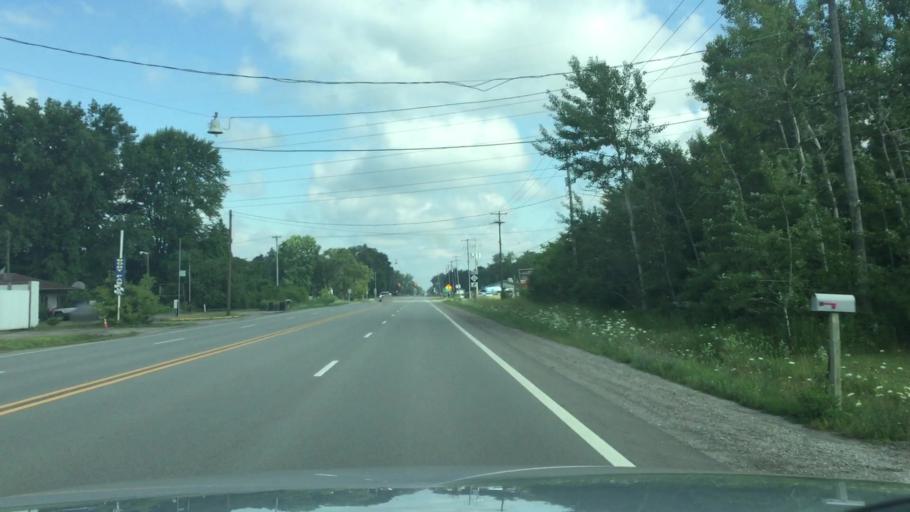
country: US
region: Michigan
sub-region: Genesee County
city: Clio
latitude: 43.2014
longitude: -83.7325
